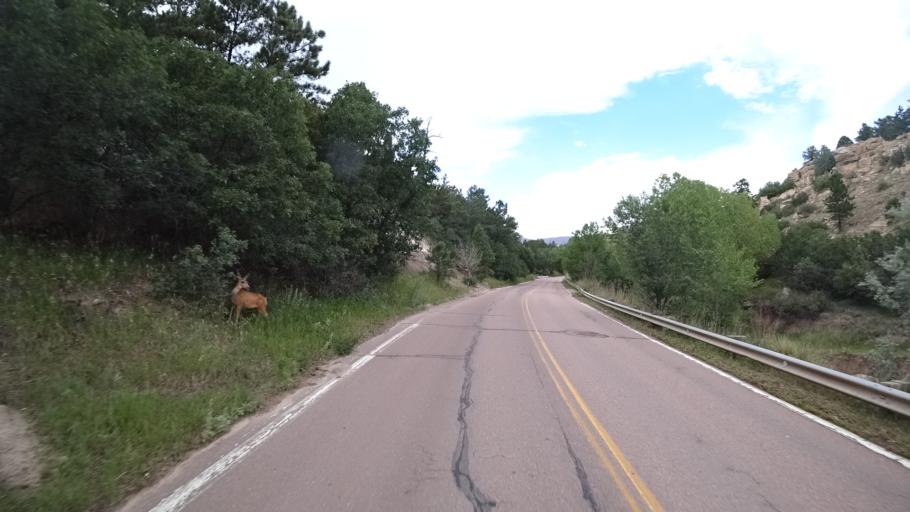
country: US
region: Colorado
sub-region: El Paso County
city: Colorado Springs
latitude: 38.9057
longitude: -104.8294
